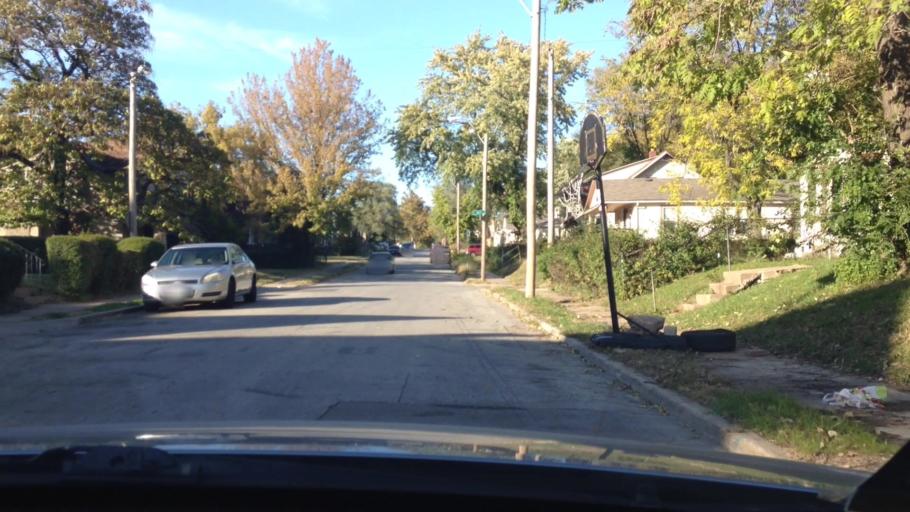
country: US
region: Missouri
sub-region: Jackson County
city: Kansas City
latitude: 39.0423
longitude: -94.5520
